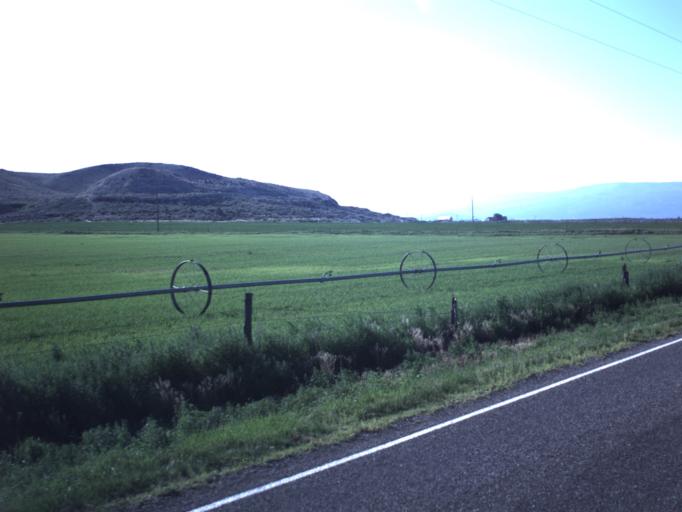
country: US
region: Utah
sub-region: Wayne County
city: Loa
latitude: 38.4286
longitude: -111.6203
